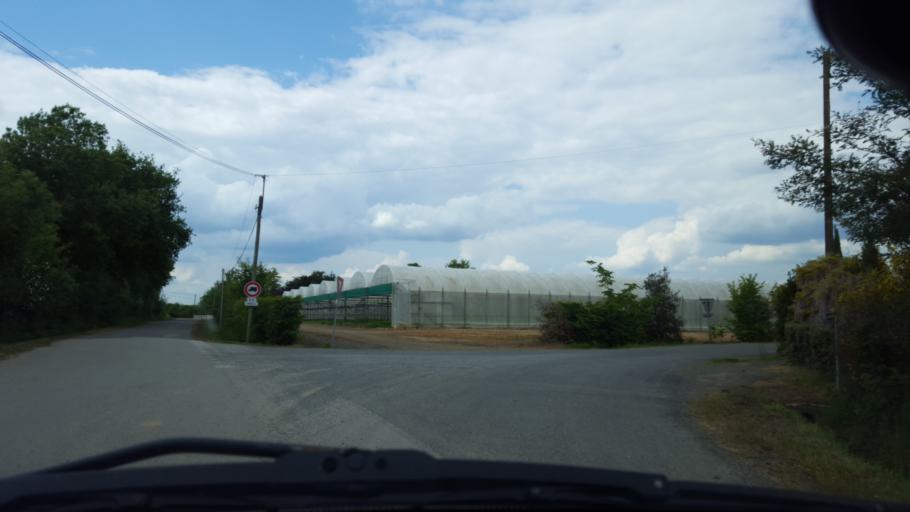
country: FR
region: Pays de la Loire
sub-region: Departement de la Loire-Atlantique
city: Saint-Philbert-de-Grand-Lieu
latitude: 47.0212
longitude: -1.6219
